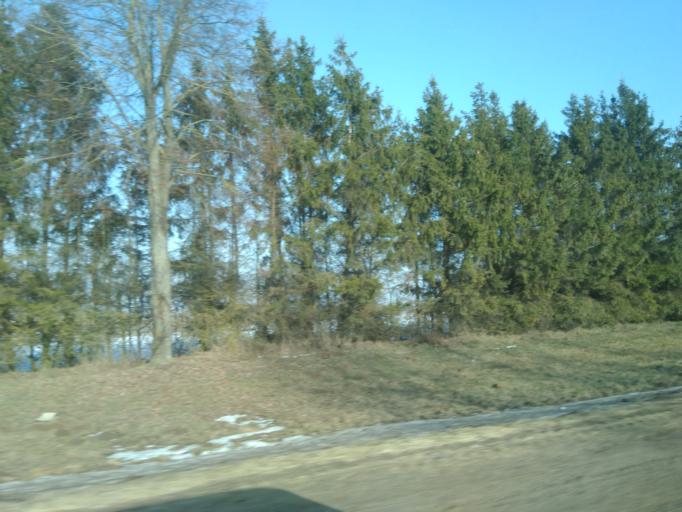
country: BY
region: Minsk
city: Snow
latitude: 53.2169
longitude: 26.4352
